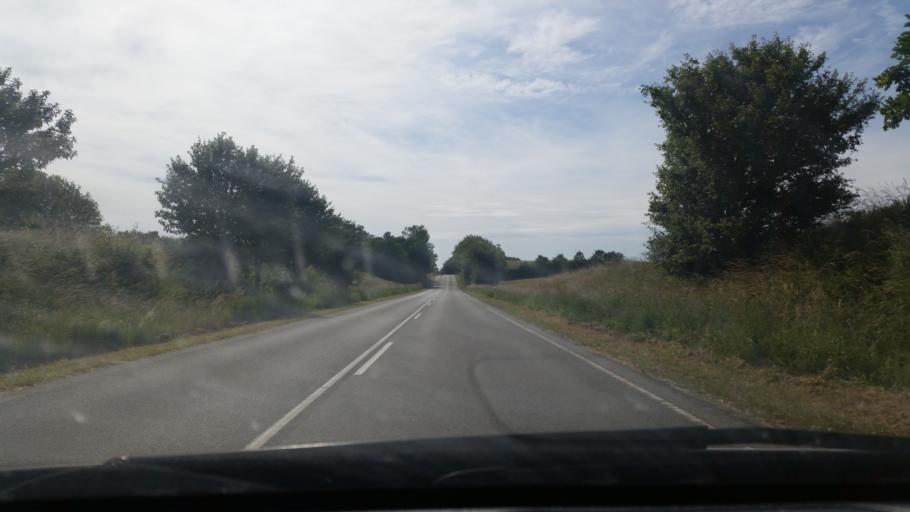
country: DK
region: Central Jutland
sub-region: Samso Kommune
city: Tranebjerg
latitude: 55.8000
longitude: 10.5421
